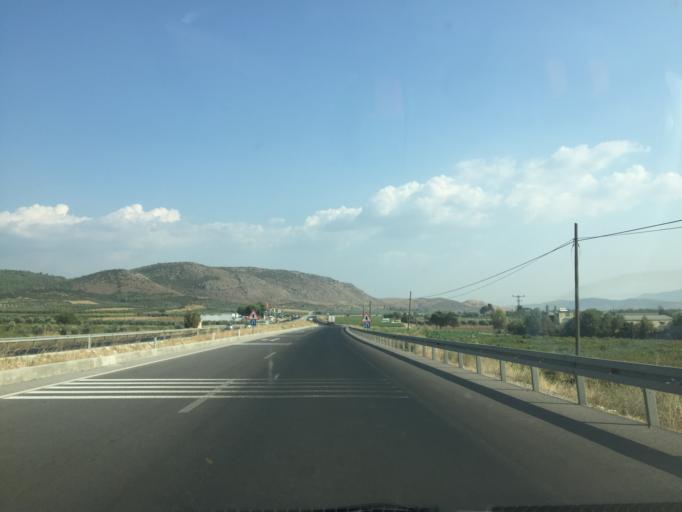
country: TR
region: Manisa
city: Golmarmara
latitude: 38.7931
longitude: 27.8990
